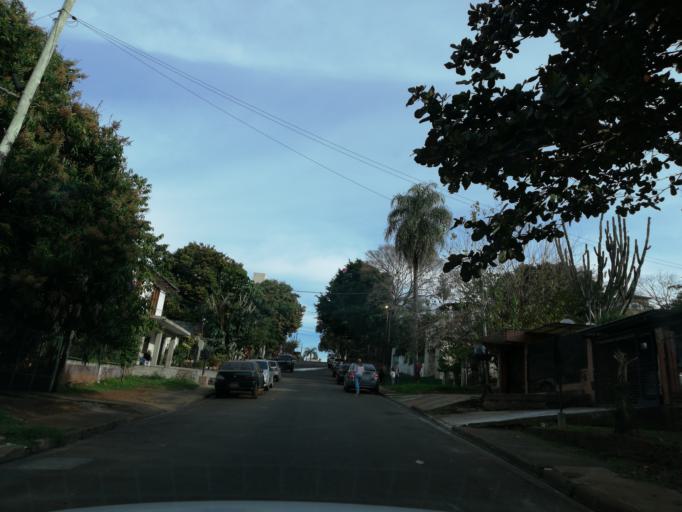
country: AR
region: Misiones
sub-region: Departamento de Capital
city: Posadas
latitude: -27.3576
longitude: -55.9139
